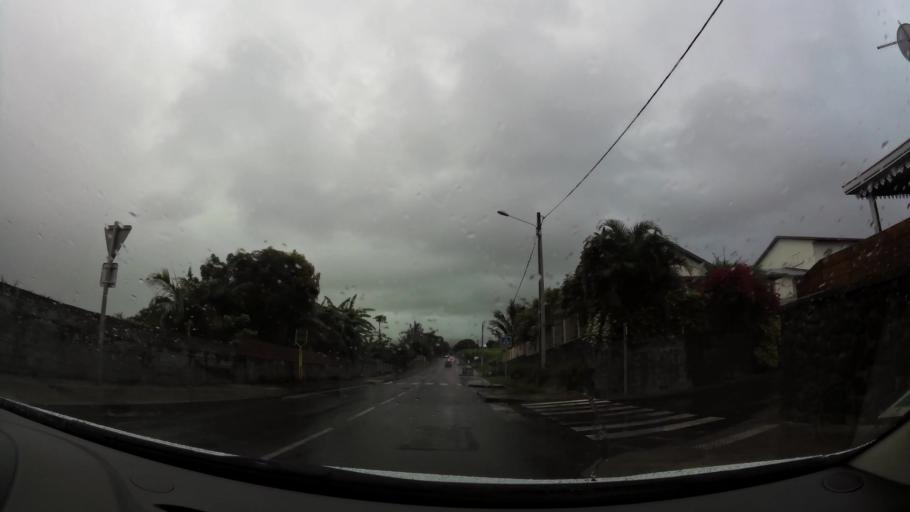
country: RE
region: Reunion
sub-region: Reunion
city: Saint-Benoit
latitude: -21.0200
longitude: 55.7011
